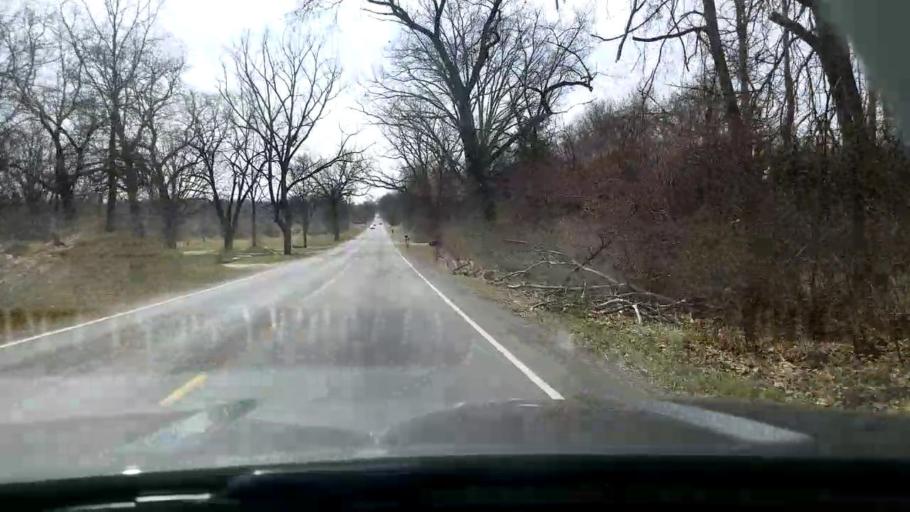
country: US
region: Michigan
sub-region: Jackson County
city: Spring Arbor
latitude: 42.2079
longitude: -84.5212
